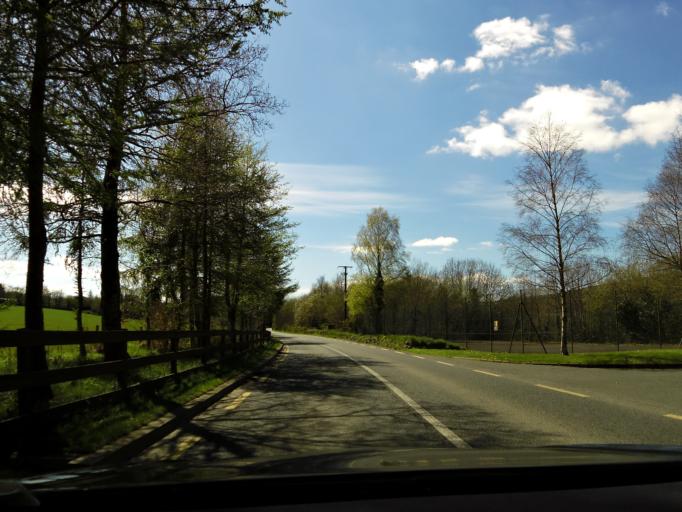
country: IE
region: Leinster
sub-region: Wicklow
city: Aughrim
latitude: 52.8523
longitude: -6.3312
